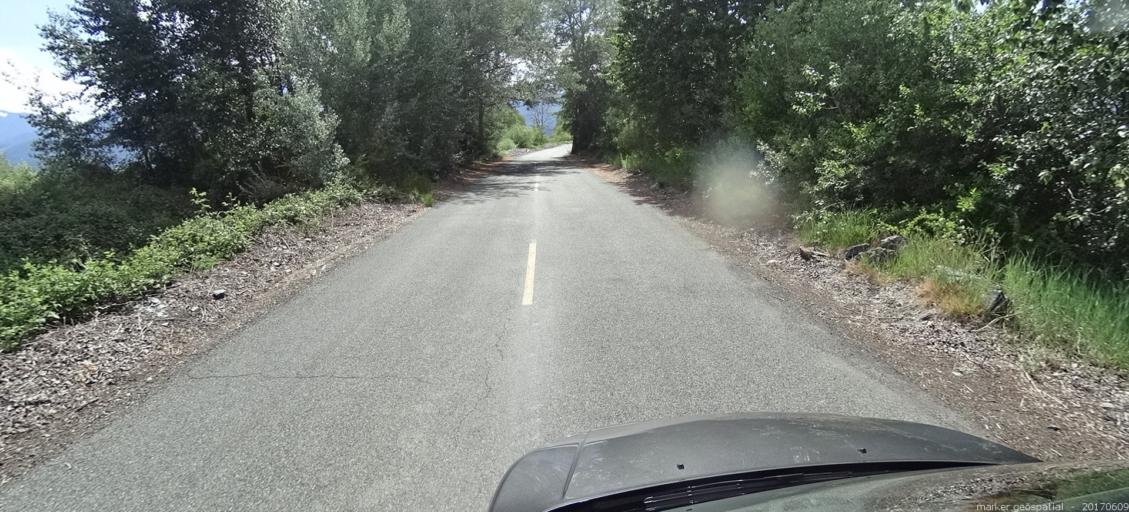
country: US
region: California
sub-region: Siskiyou County
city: Yreka
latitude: 41.5148
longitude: -122.8712
